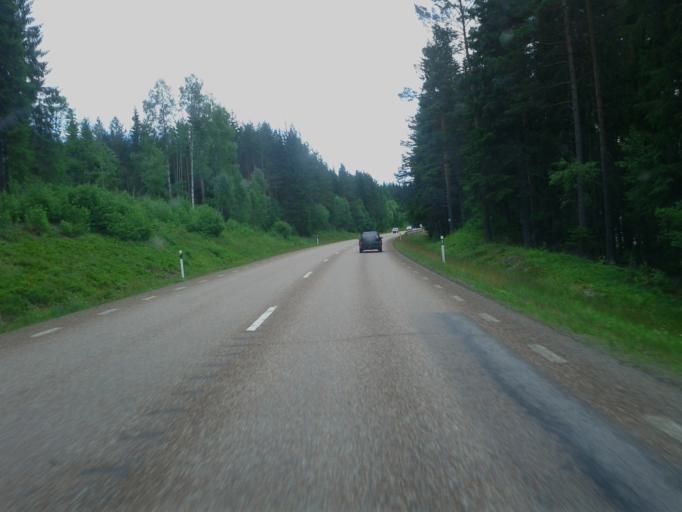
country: SE
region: Dalarna
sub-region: Faluns Kommun
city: Bjursas
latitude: 60.7770
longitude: 15.3160
